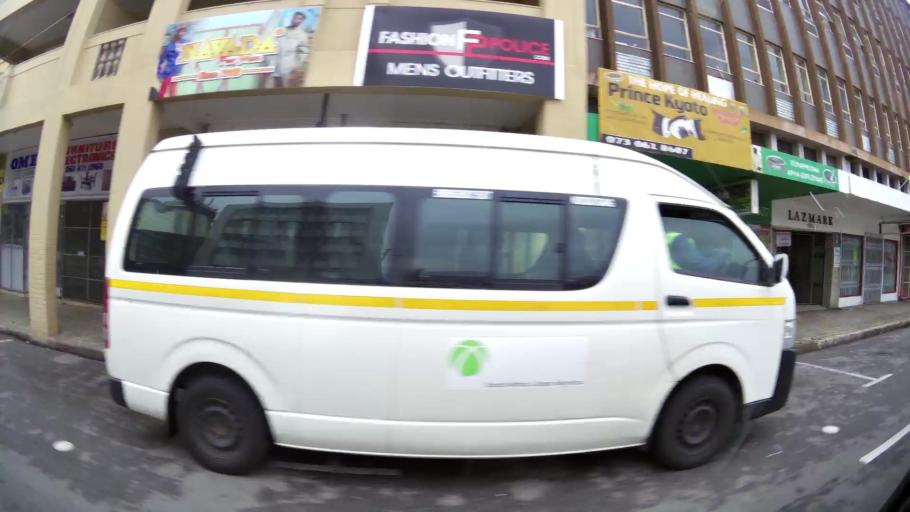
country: ZA
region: Eastern Cape
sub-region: Nelson Mandela Bay Metropolitan Municipality
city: Port Elizabeth
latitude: -33.9483
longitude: 25.6069
